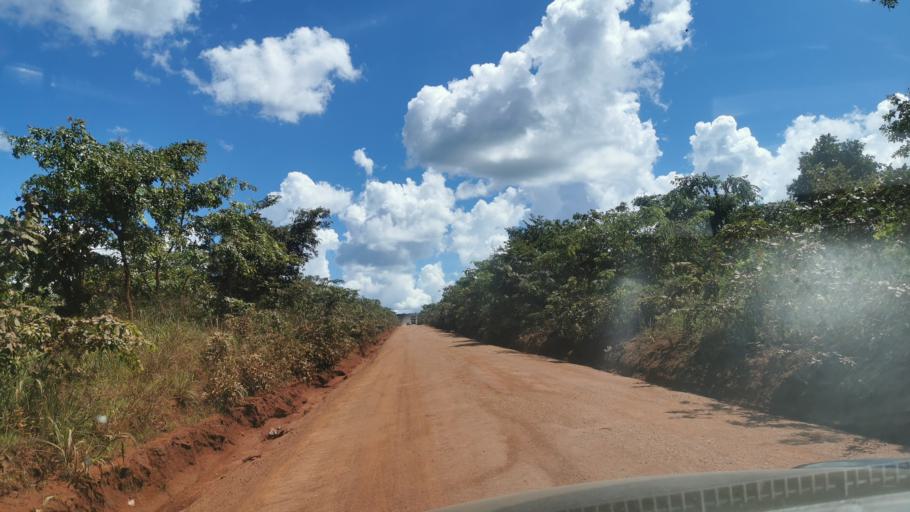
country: TZ
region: Kagera
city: Biharamulo
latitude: -2.9871
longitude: 31.2198
